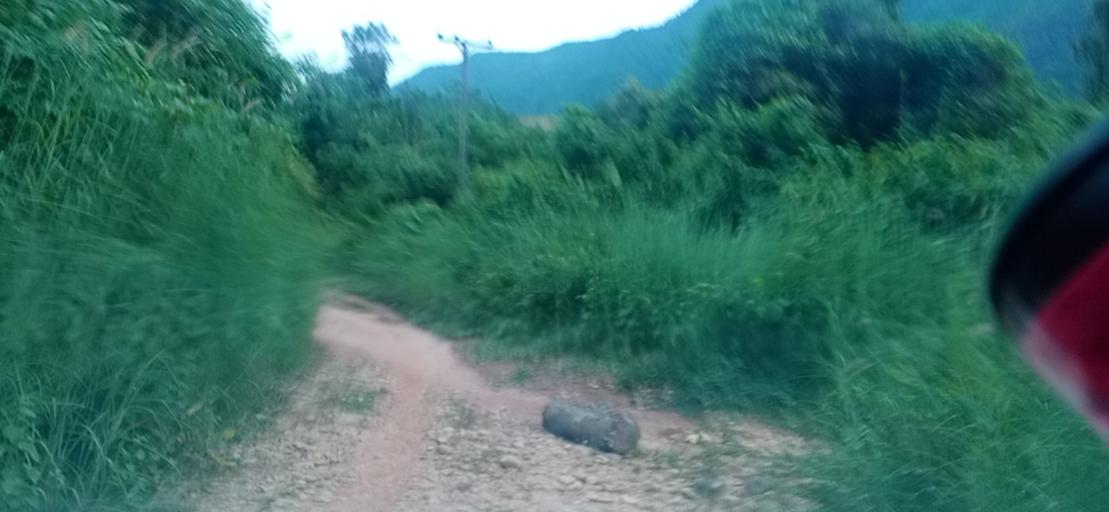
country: TH
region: Changwat Bueng Kan
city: Pak Khat
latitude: 18.5630
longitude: 103.2754
